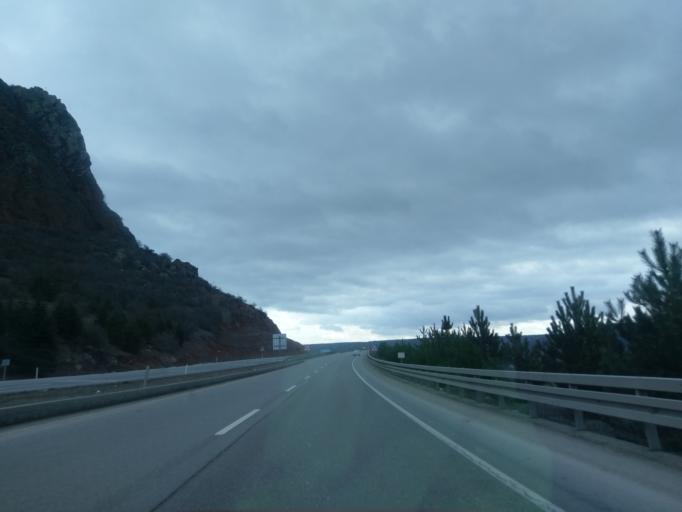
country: TR
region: Kuetahya
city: Sabuncu
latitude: 39.5753
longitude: 30.0938
